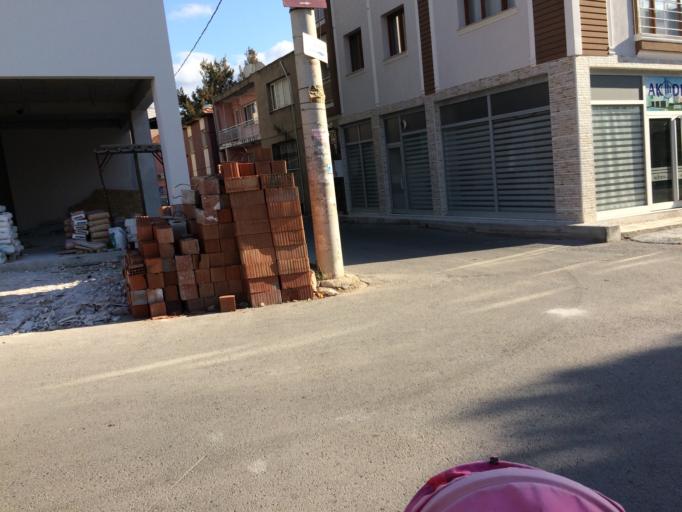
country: TR
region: Izmir
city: Karsiyaka
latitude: 38.4915
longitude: 27.0588
